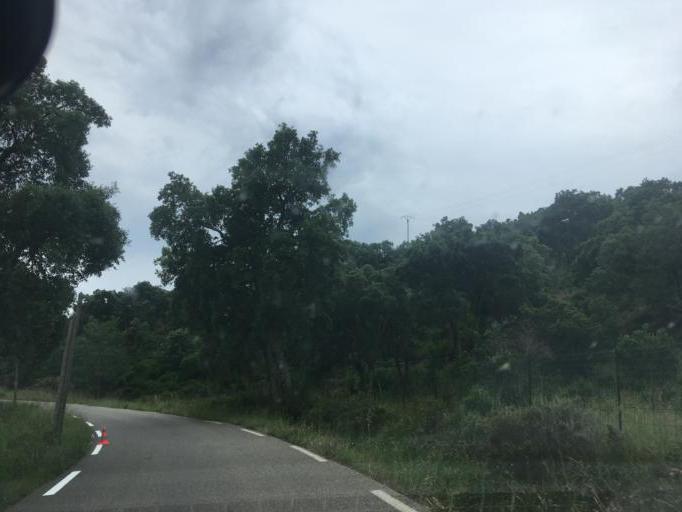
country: FR
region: Provence-Alpes-Cote d'Azur
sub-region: Departement du Var
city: La Londe-les-Maures
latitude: 43.1790
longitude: 6.2132
